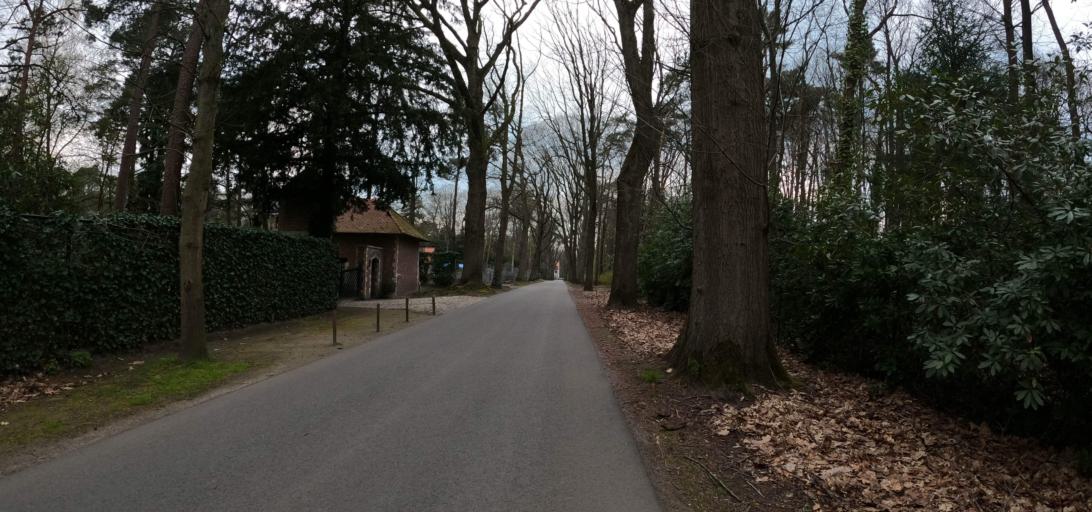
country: BE
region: Flanders
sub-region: Provincie Antwerpen
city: Kalmthout
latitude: 51.3558
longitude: 4.4655
